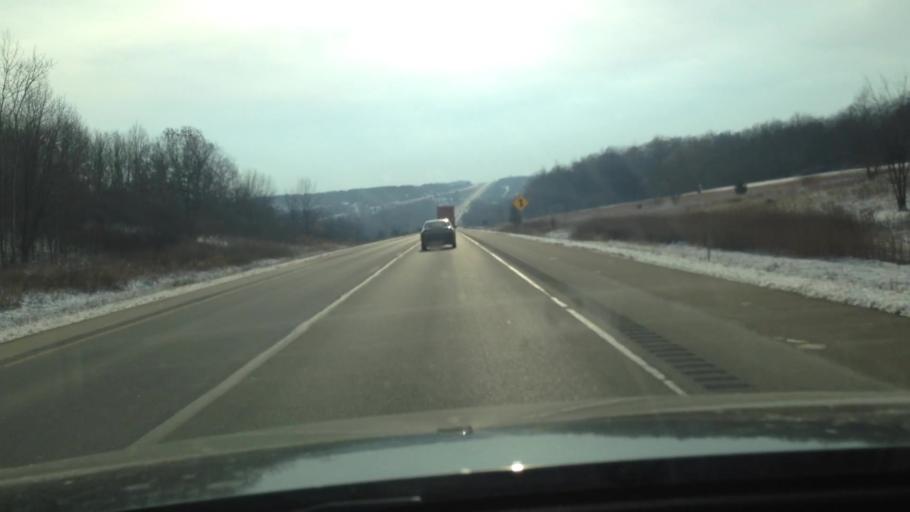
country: US
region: Wisconsin
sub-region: Walworth County
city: East Troy
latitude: 42.7333
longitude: -88.4599
